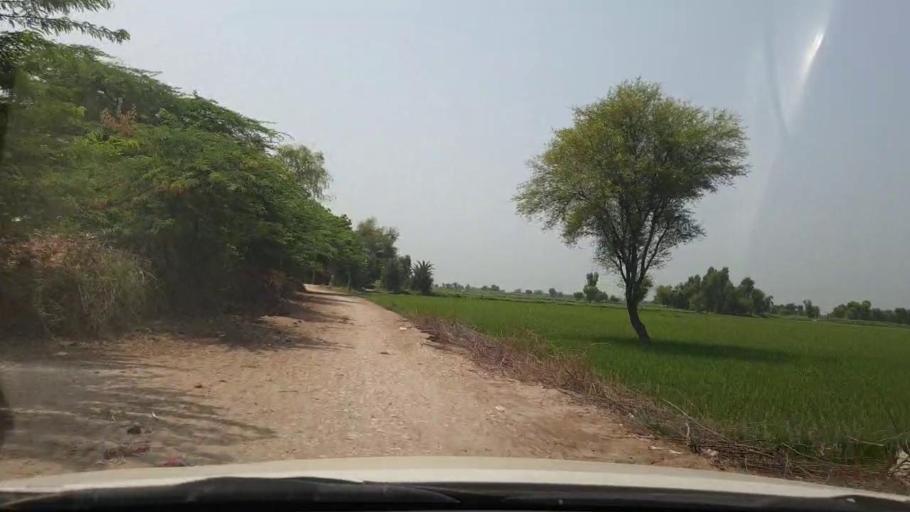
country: PK
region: Sindh
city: Rustam jo Goth
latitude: 27.9761
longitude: 68.7217
